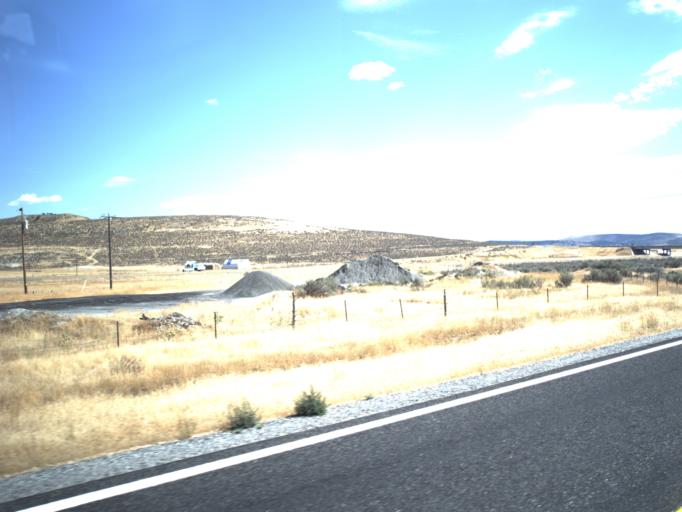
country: US
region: Idaho
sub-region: Oneida County
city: Malad City
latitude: 41.9658
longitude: -112.7679
